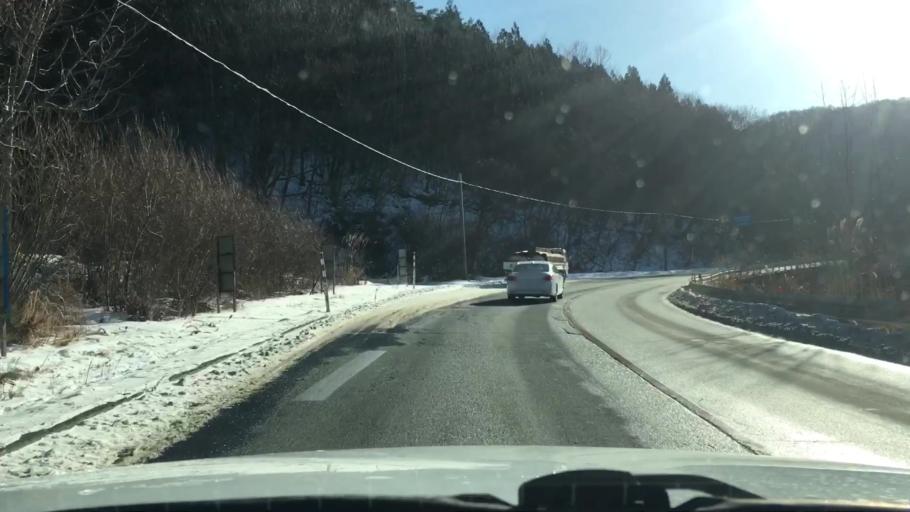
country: JP
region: Iwate
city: Morioka-shi
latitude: 39.6577
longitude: 141.3395
